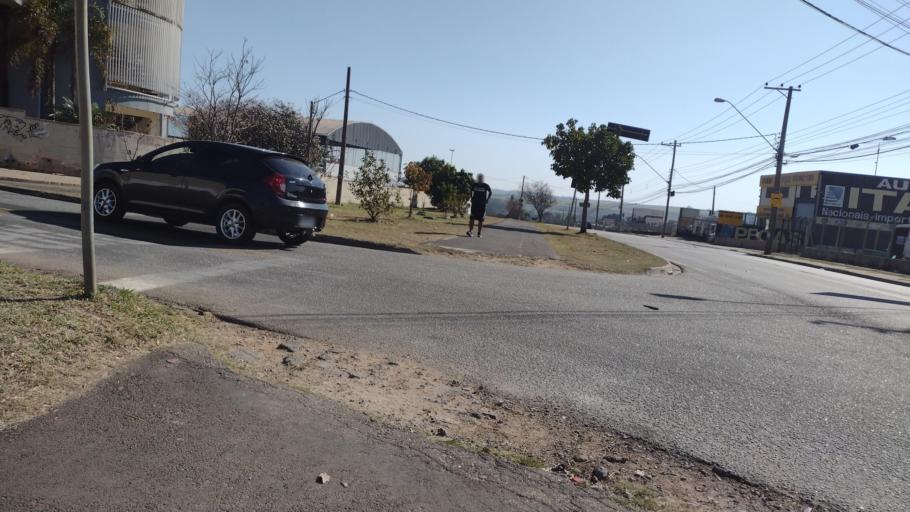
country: BR
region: Sao Paulo
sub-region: Sorocaba
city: Sorocaba
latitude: -23.4237
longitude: -47.4823
